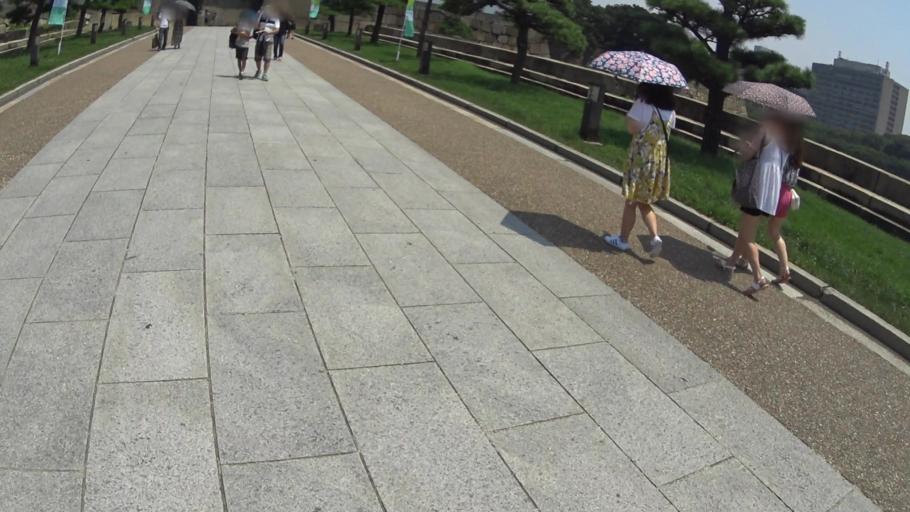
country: JP
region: Osaka
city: Osaka-shi
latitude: 34.6852
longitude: 135.5219
